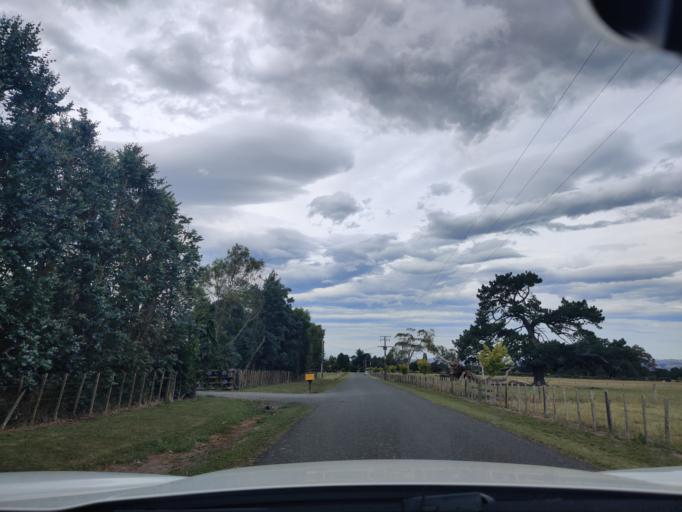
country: NZ
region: Wellington
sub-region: Masterton District
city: Masterton
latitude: -41.0365
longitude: 175.4414
